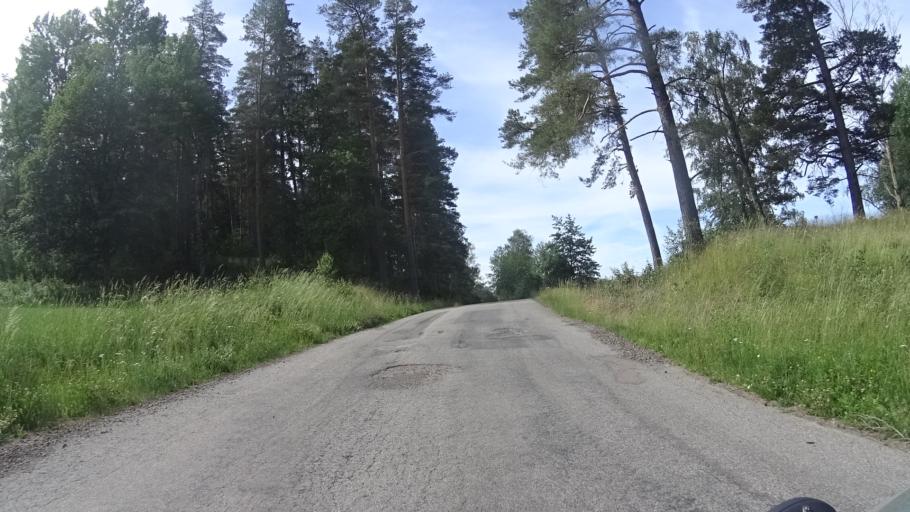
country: SE
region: Kalmar
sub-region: Vasterviks Kommun
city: Overum
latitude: 57.8762
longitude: 16.1750
